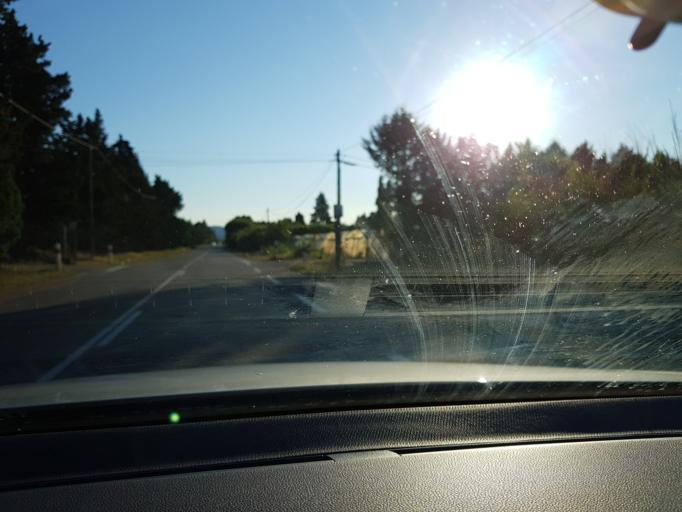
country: FR
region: Provence-Alpes-Cote d'Azur
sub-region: Departement des Bouches-du-Rhone
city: Molleges
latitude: 43.7959
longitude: 4.9886
